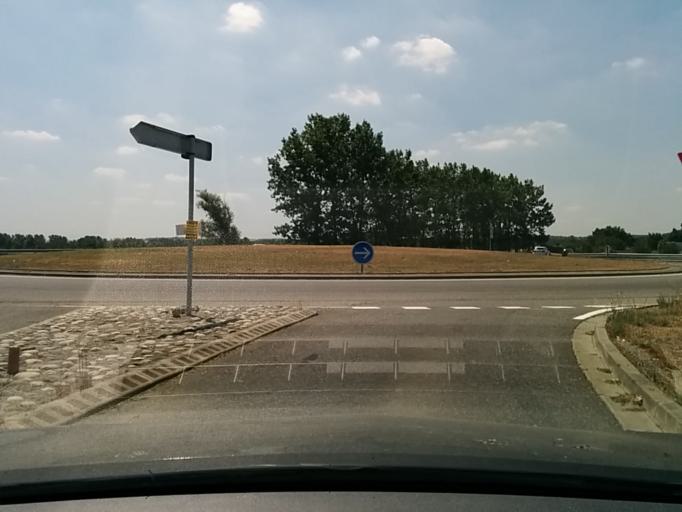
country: FR
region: Midi-Pyrenees
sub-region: Departement de la Haute-Garonne
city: Labege
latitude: 43.5159
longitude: 1.5350
